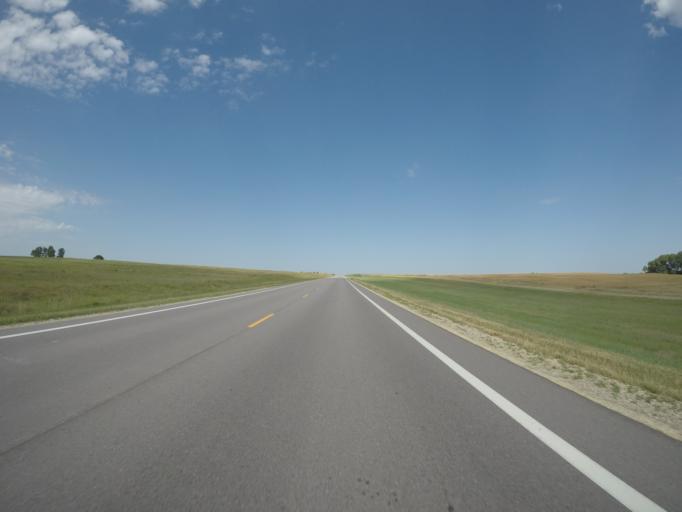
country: US
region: Kansas
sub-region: Clay County
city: Clay Center
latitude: 39.3788
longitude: -97.3154
